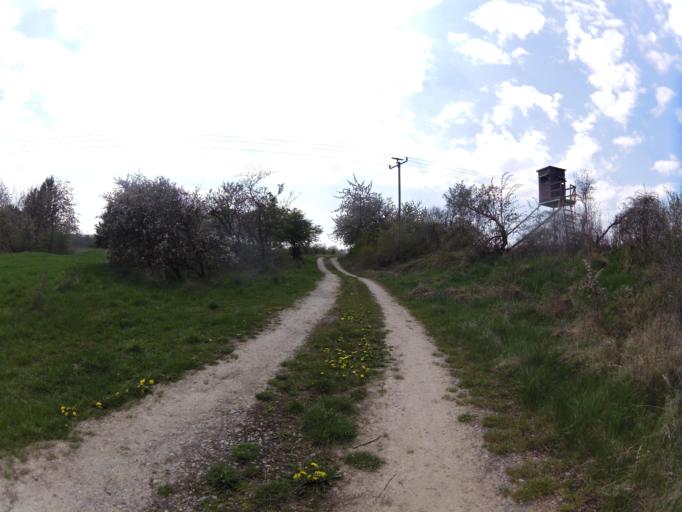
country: DE
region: Bavaria
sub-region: Regierungsbezirk Unterfranken
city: Sommerhausen
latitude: 49.6804
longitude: 10.0190
